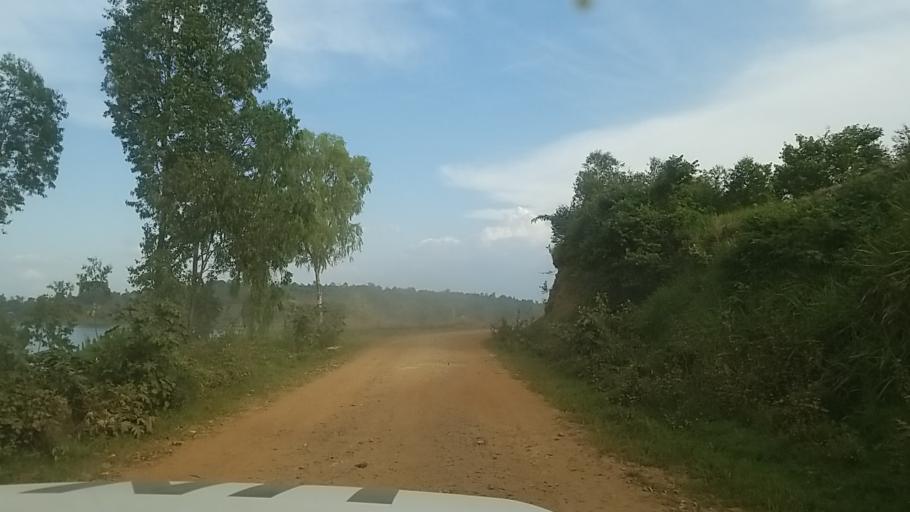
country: RW
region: Western Province
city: Cyangugu
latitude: -2.1081
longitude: 28.9058
